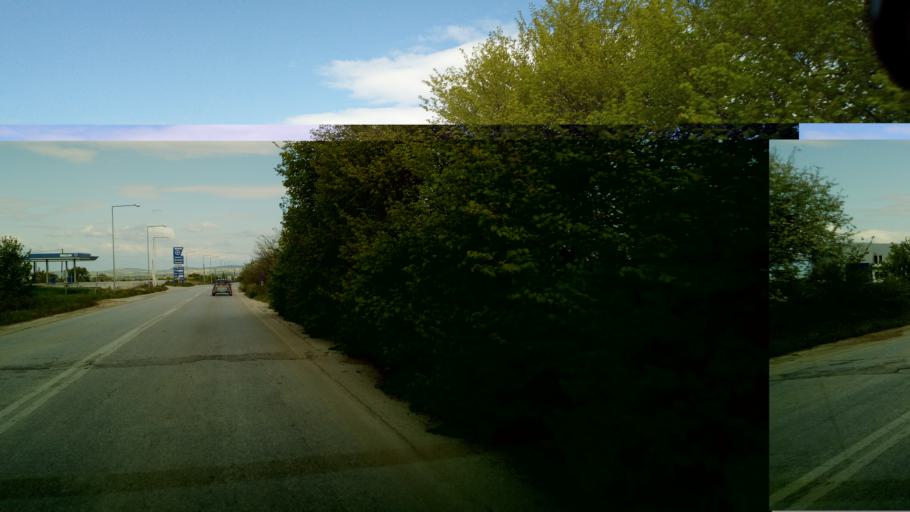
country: GR
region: Central Macedonia
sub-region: Nomos Kilkis
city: Nea Santa
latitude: 40.8198
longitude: 22.9313
